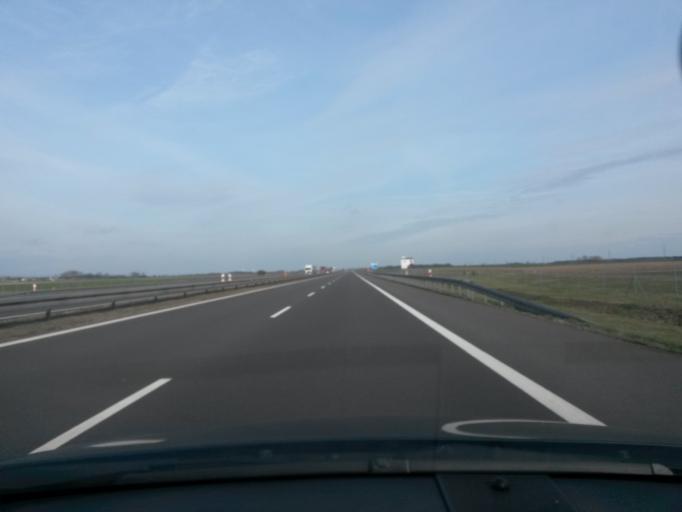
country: PL
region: Greater Poland Voivodeship
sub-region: Powiat sredzki
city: Dominowo
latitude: 52.3099
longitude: 17.3039
